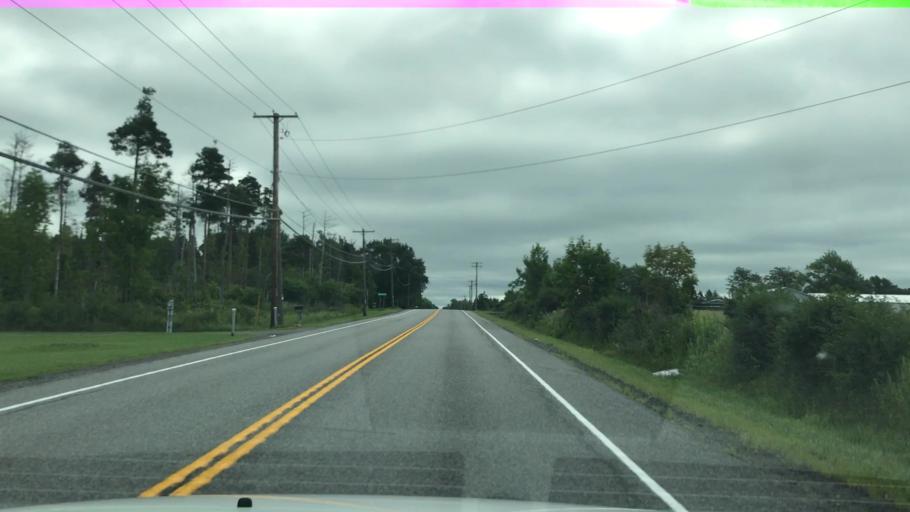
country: US
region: New York
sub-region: Wyoming County
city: Attica
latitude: 42.8360
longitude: -78.3668
